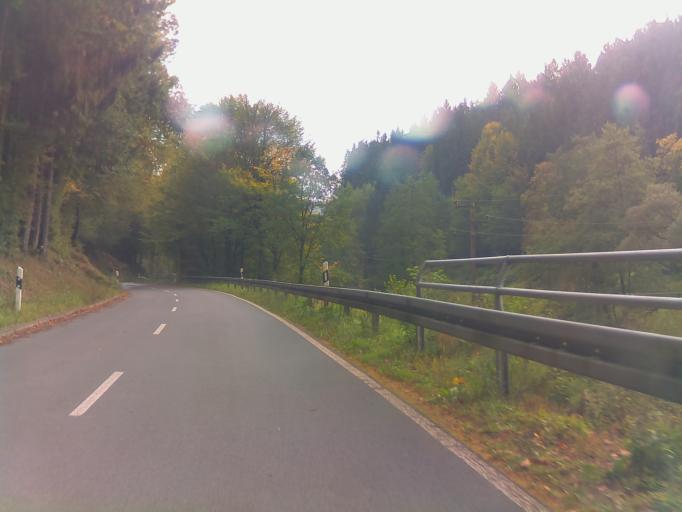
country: DE
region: Bavaria
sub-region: Regierungsbezirk Unterfranken
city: Kirchzell
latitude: 49.6249
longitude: 9.1399
